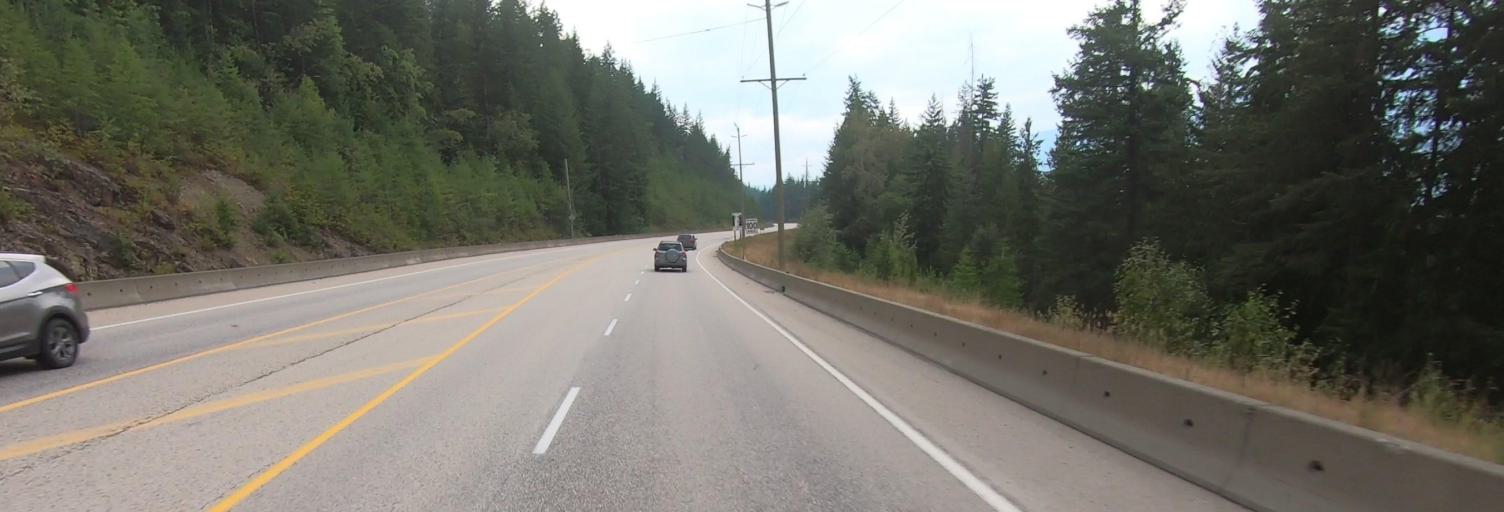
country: CA
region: British Columbia
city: Sicamous
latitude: 50.7893
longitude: -119.0915
